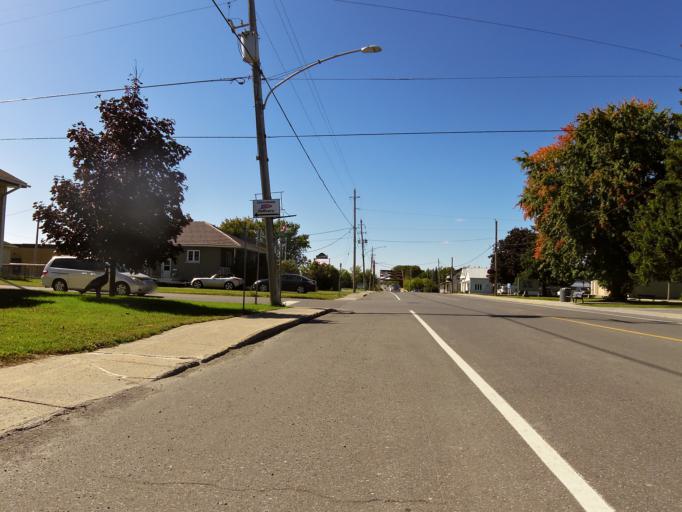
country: CA
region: Ontario
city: Casselman
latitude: 45.2548
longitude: -75.1229
